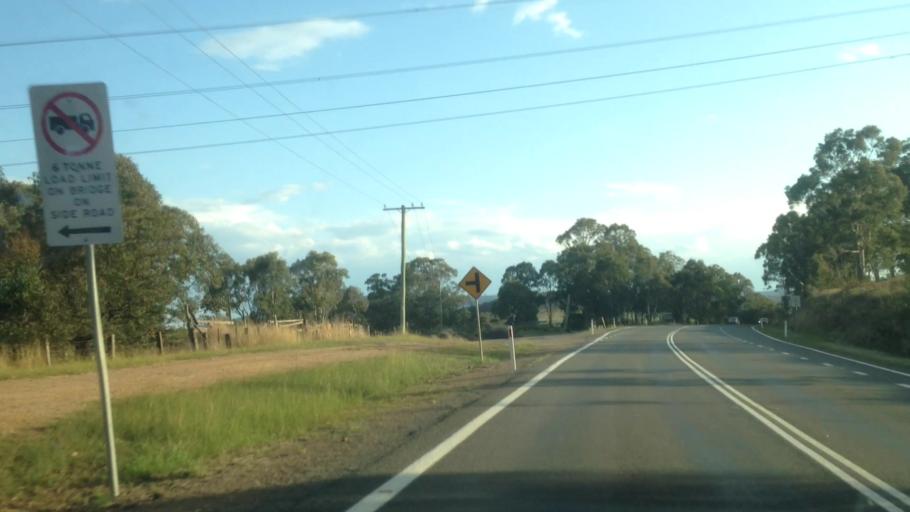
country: AU
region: New South Wales
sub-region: Cessnock
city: Kurri Kurri
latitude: -32.8708
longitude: 151.4788
